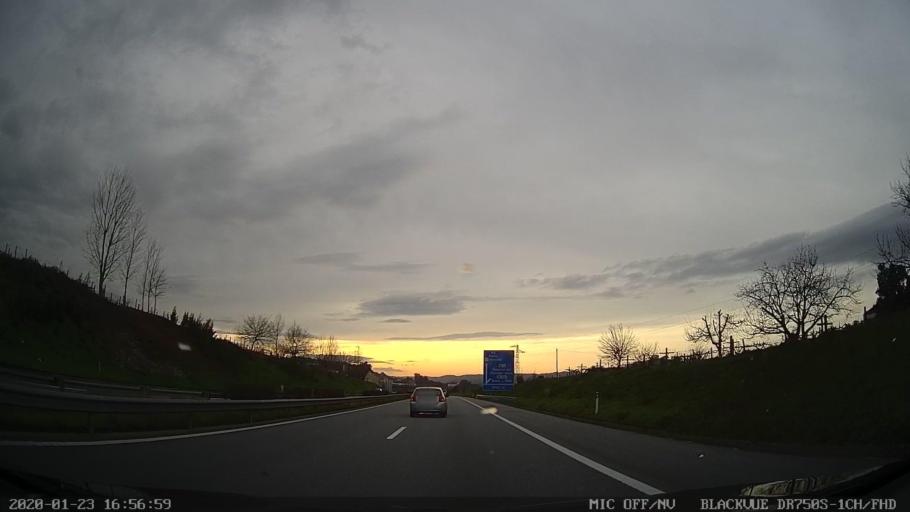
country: PT
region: Porto
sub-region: Penafiel
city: Penafiel
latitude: 41.2063
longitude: -8.2953
